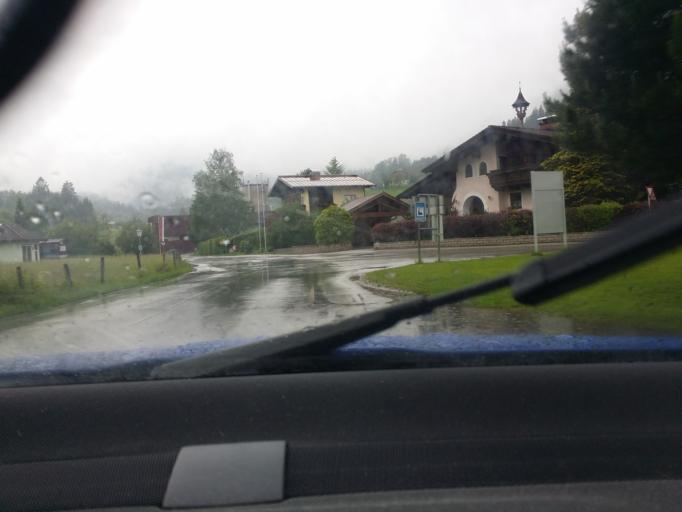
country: AT
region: Salzburg
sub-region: Politischer Bezirk Hallein
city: Abtenau
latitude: 47.5941
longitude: 13.3133
